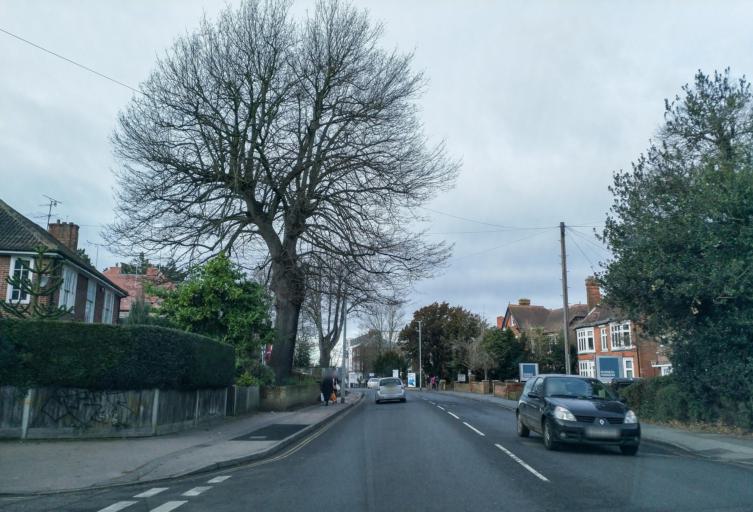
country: GB
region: England
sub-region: Kent
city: Canterbury
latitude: 51.2741
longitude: 1.0889
